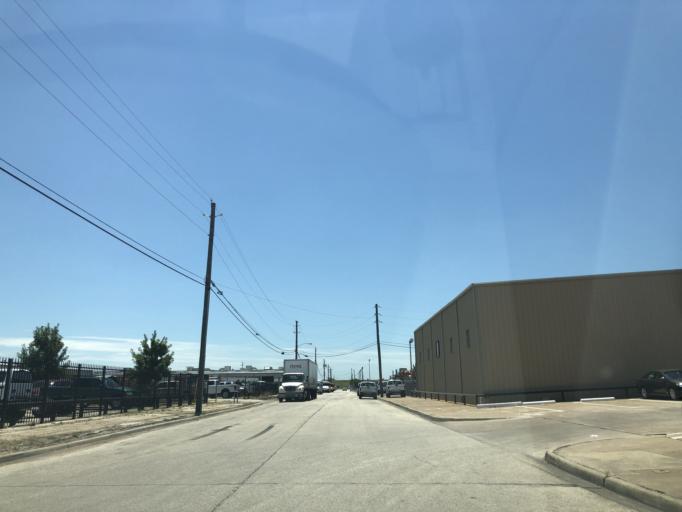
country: US
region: Texas
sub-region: Dallas County
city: Irving
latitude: 32.8076
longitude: -96.8859
